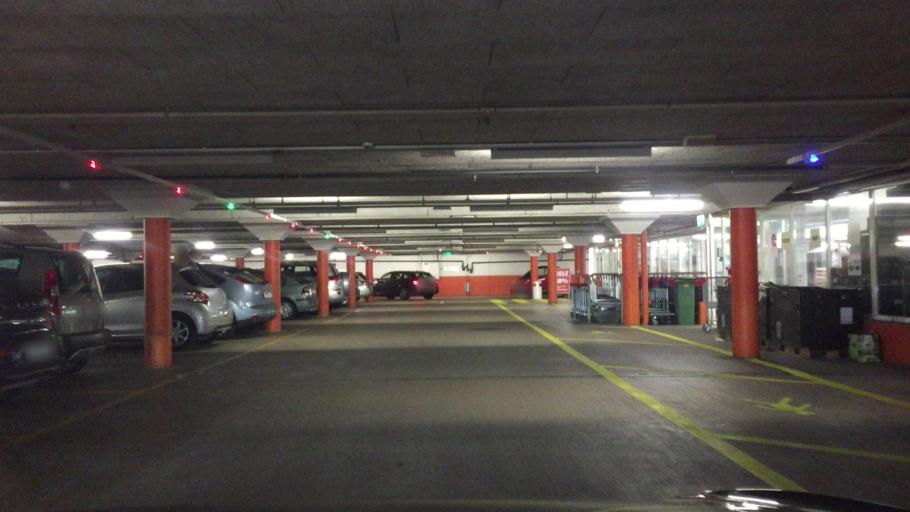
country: CH
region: Vaud
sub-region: Ouest Lausannois District
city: Renens
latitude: 46.5328
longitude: 6.5864
